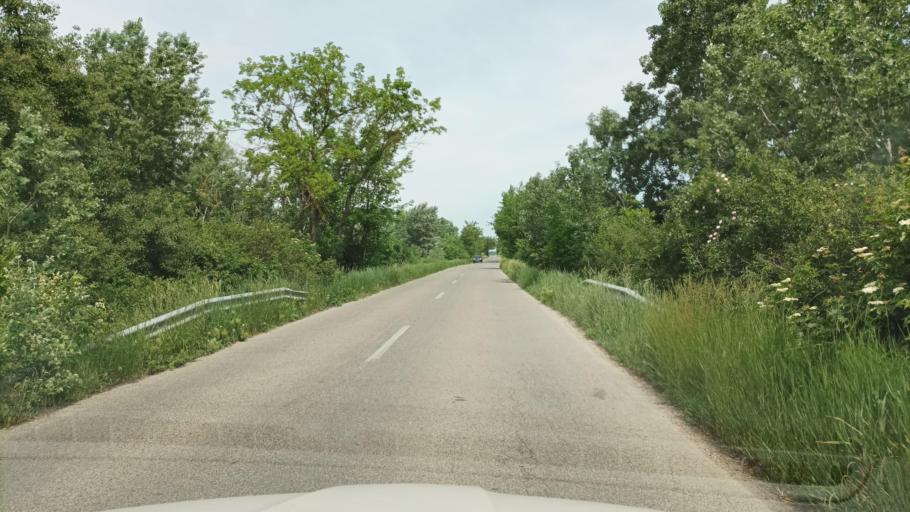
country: HU
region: Pest
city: Rackeve
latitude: 47.0973
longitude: 18.9273
